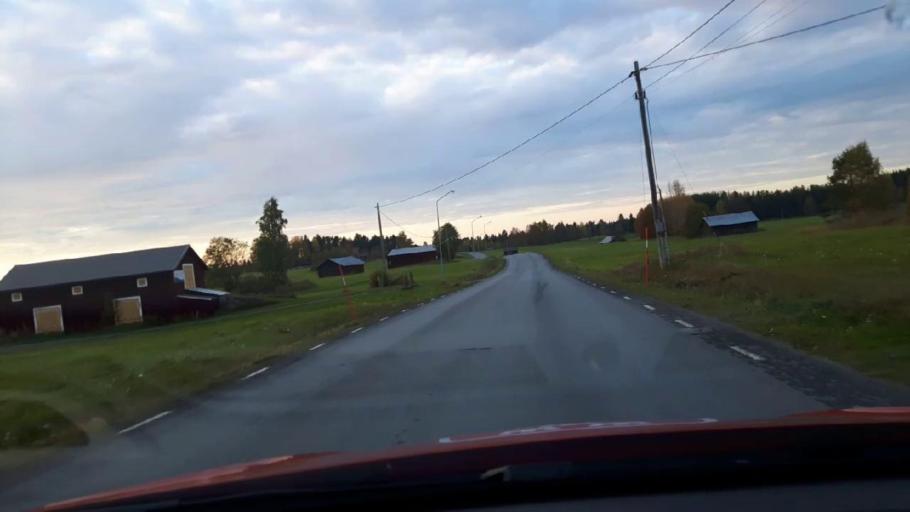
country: SE
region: Jaemtland
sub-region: OEstersunds Kommun
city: Lit
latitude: 63.3097
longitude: 14.9966
